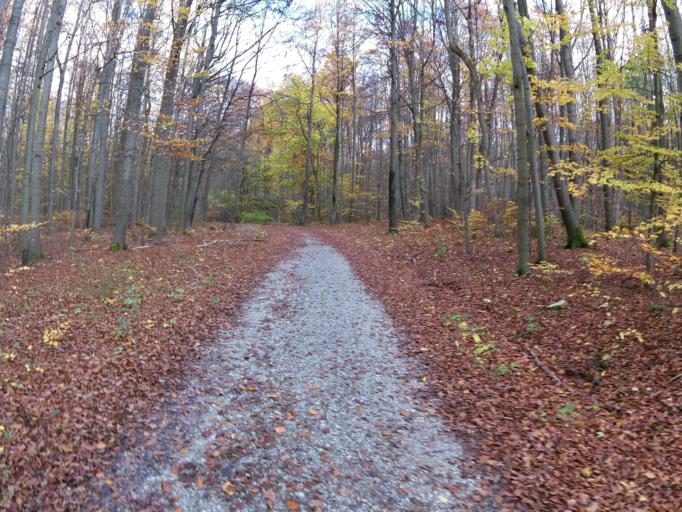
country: DE
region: Thuringia
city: Kammerforst
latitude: 51.0807
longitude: 10.4018
